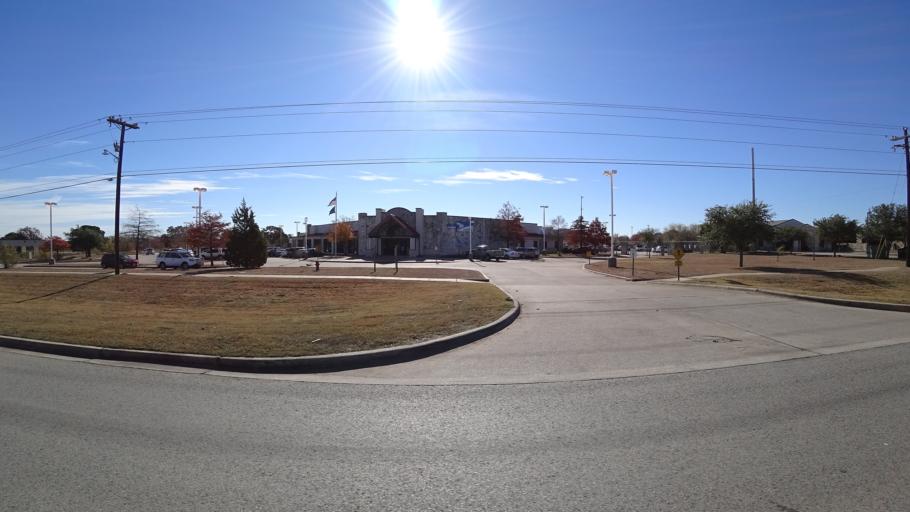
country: US
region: Texas
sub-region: Williamson County
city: Cedar Park
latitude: 30.5224
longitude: -97.8254
